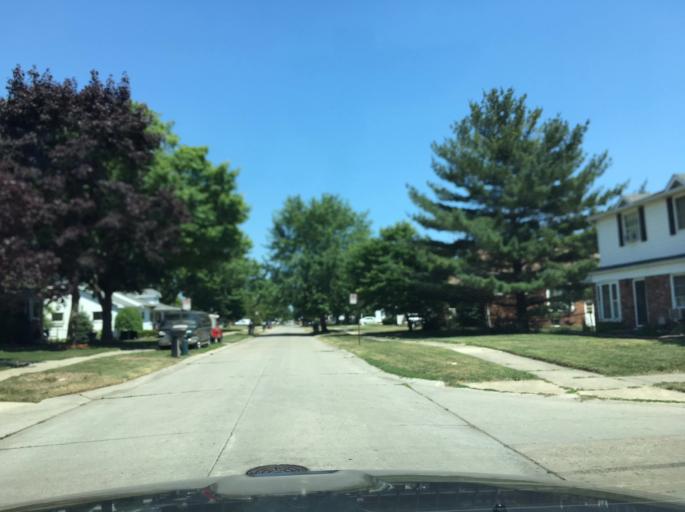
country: US
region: Michigan
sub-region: Macomb County
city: Fraser
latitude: 42.5427
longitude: -82.9167
